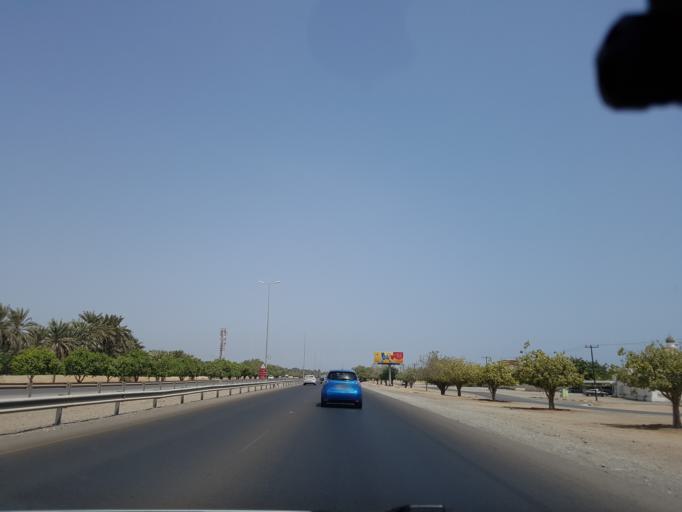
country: OM
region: Al Batinah
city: Saham
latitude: 24.1715
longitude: 56.8598
